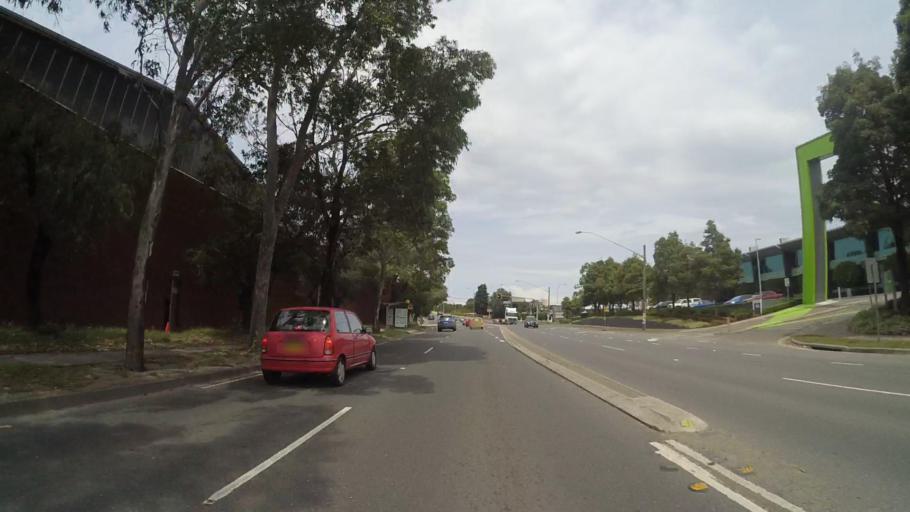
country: AU
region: New South Wales
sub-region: Botany Bay
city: Mascot
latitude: -33.9189
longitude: 151.1777
